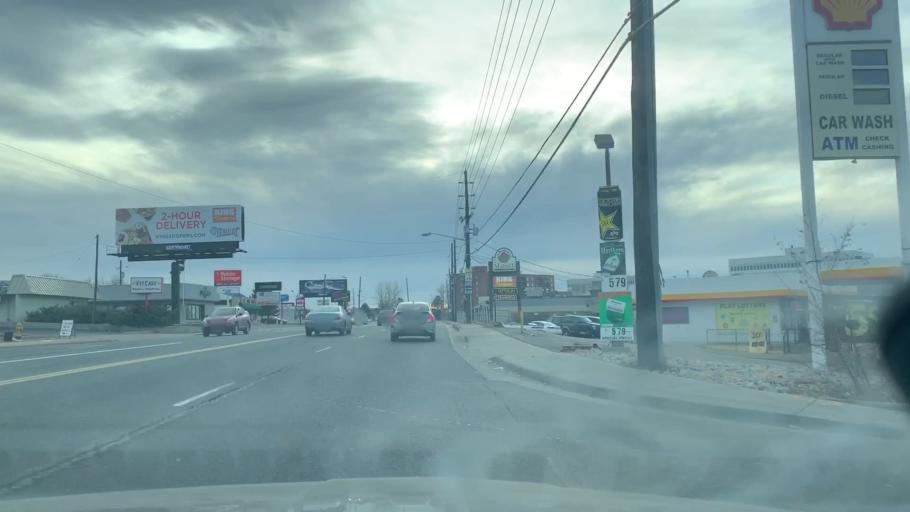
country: US
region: Colorado
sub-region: Arapahoe County
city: Glendale
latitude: 39.7026
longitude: -104.9126
